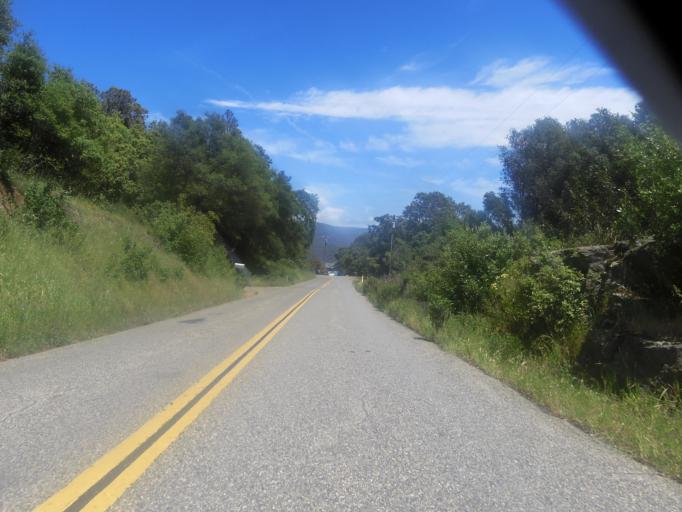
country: US
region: California
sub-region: Mariposa County
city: Midpines
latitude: 37.5108
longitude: -119.9085
